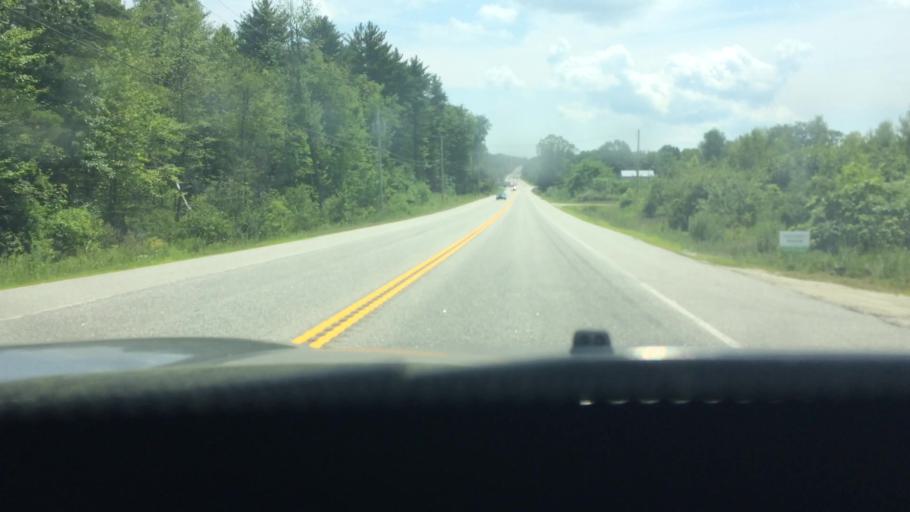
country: US
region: Maine
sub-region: Androscoggin County
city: Poland
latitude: 44.0192
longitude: -70.3636
